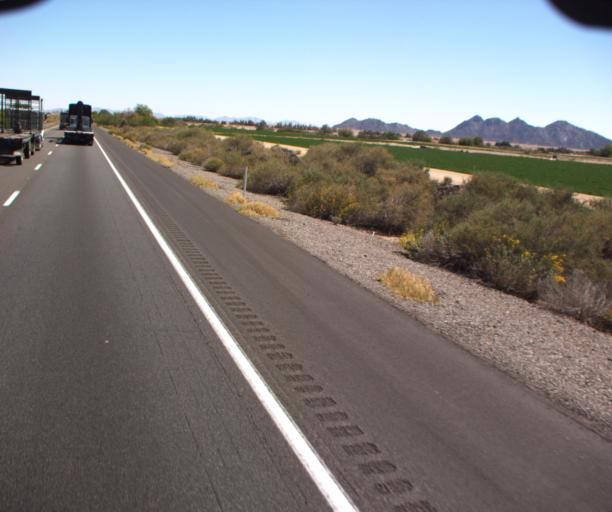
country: US
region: Arizona
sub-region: Yuma County
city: Wellton
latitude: 32.6751
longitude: -114.0626
